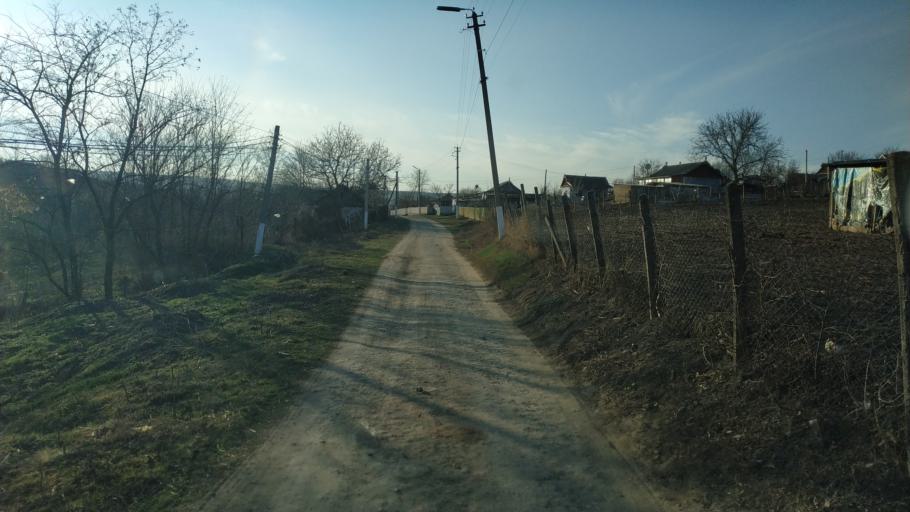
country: MD
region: Hincesti
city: Hincesti
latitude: 46.6992
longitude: 28.5379
